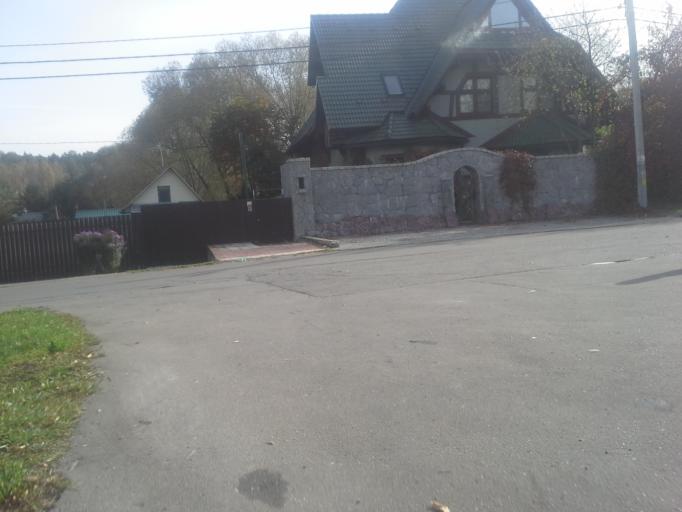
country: RU
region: Moskovskaya
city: Gorki Vtoryye
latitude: 55.6778
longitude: 37.1531
